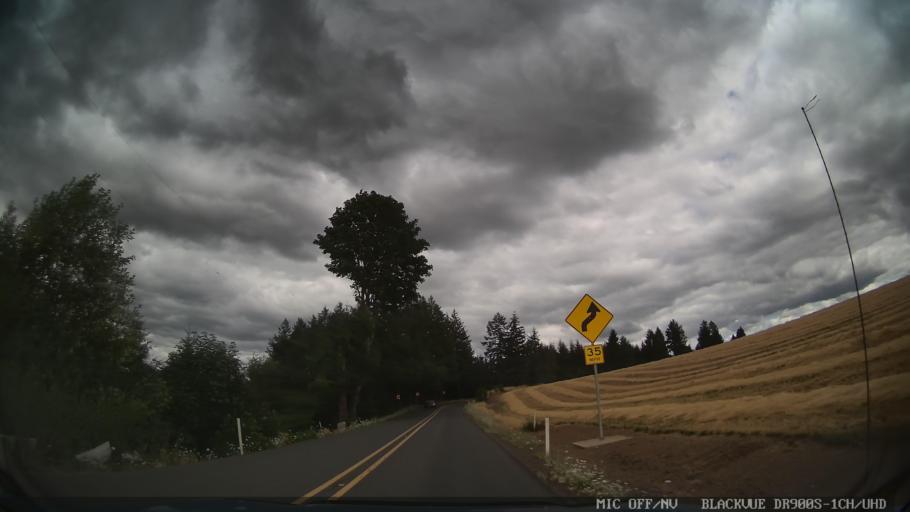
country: US
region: Oregon
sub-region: Linn County
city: Lyons
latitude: 44.8533
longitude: -122.6815
